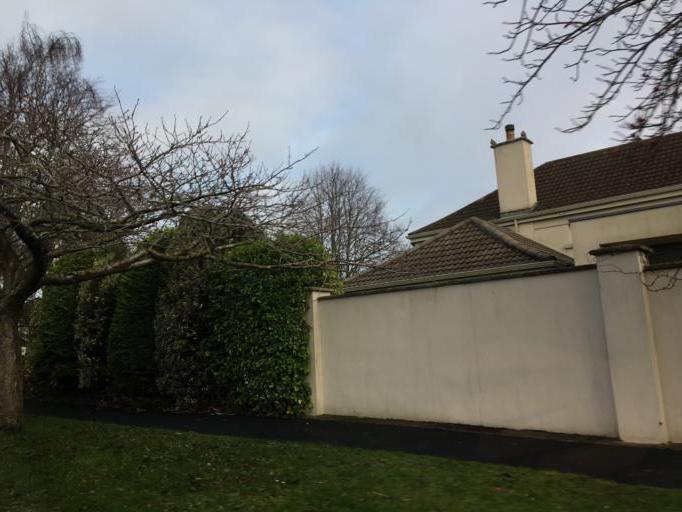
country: IE
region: Leinster
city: Castleknock
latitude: 53.3689
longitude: -6.3582
